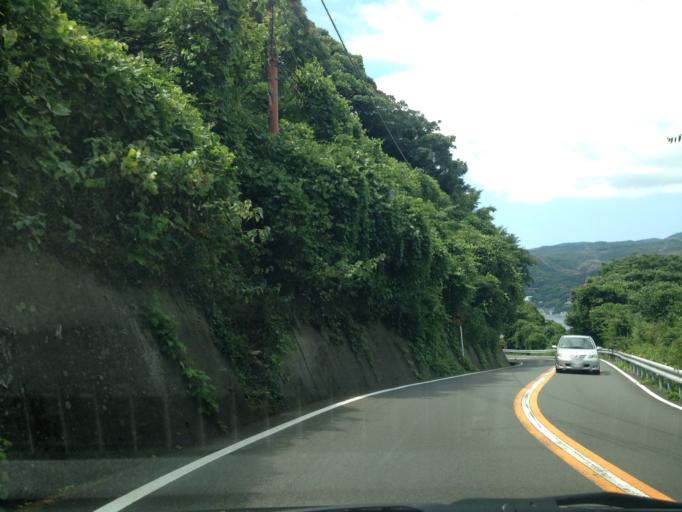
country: JP
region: Shizuoka
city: Shimoda
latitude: 34.6559
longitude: 138.7923
